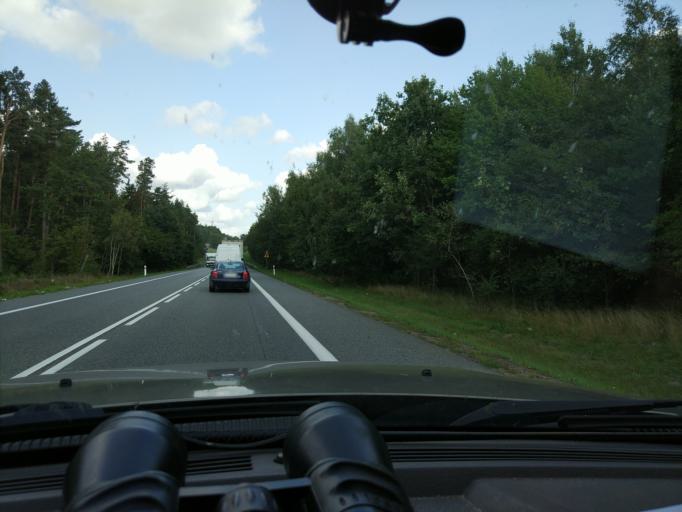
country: PL
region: Masovian Voivodeship
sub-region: Powiat mlawski
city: Mlawa
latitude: 53.1418
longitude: 20.3990
